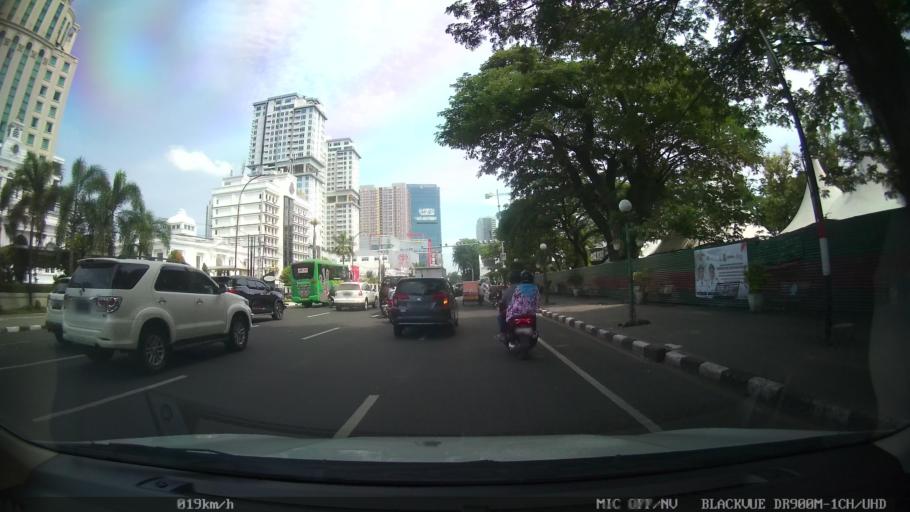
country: ID
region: North Sumatra
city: Medan
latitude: 3.5901
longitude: 98.6779
